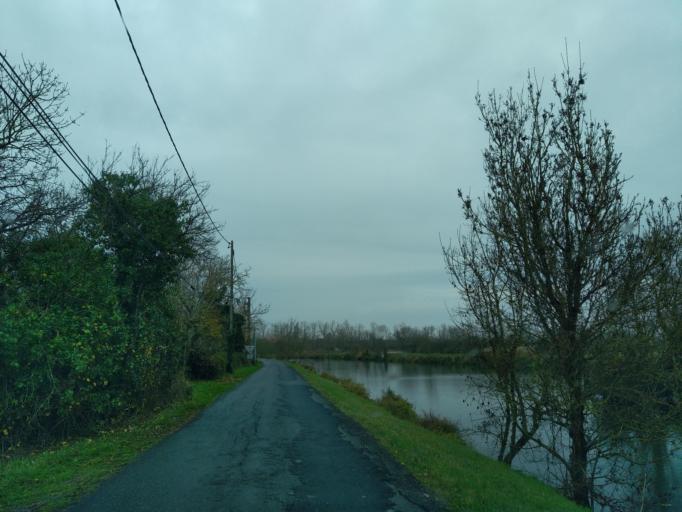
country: FR
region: Pays de la Loire
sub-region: Departement de la Vendee
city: Maillezais
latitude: 46.3207
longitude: -0.7861
